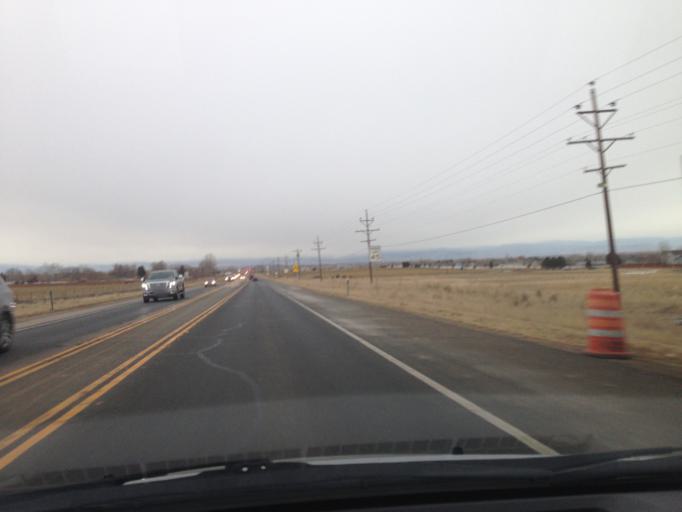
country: US
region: Colorado
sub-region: Weld County
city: Dacono
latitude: 40.0877
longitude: -104.9195
